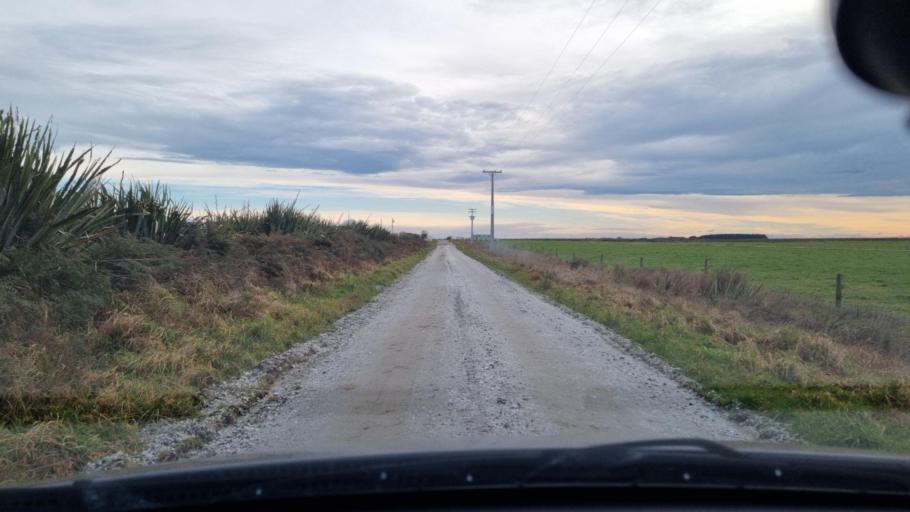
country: NZ
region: Southland
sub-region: Invercargill City
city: Bluff
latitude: -46.5309
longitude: 168.3836
